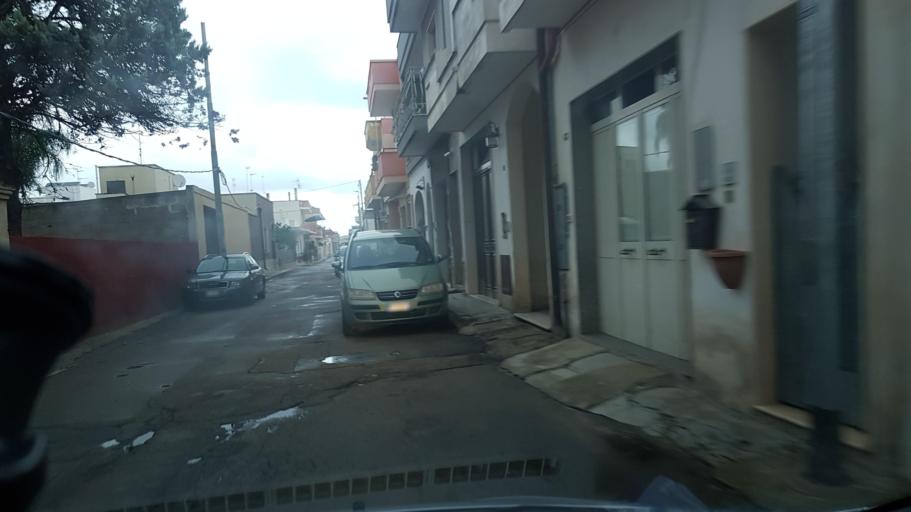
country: IT
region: Apulia
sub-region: Provincia di Lecce
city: Carmiano
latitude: 40.3394
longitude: 18.0405
